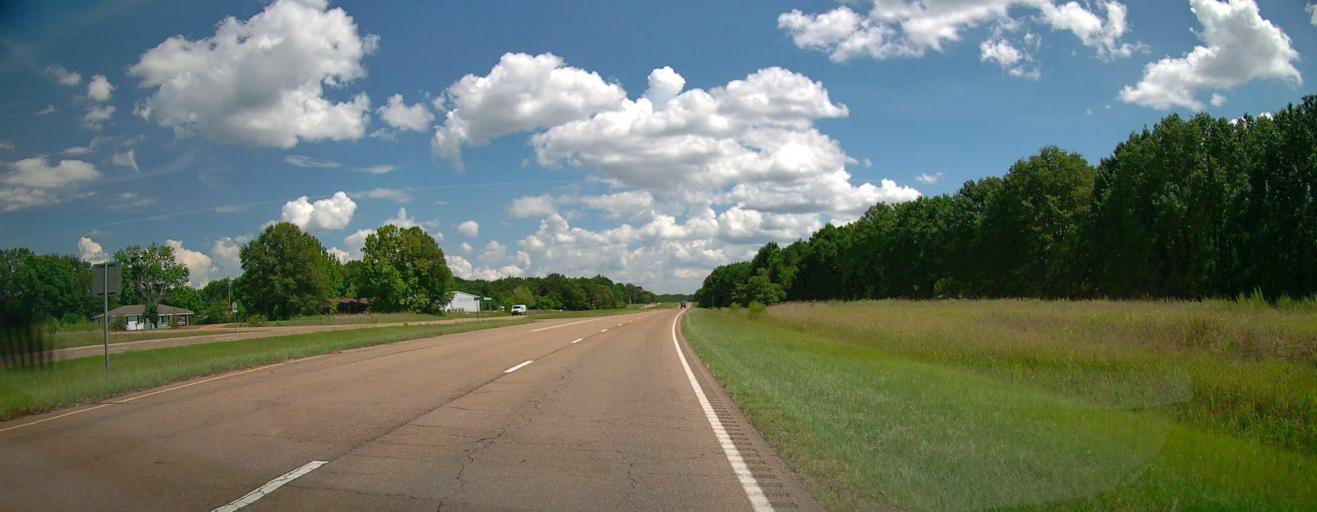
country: US
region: Mississippi
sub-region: Monroe County
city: Aberdeen
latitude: 33.8020
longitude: -88.4654
